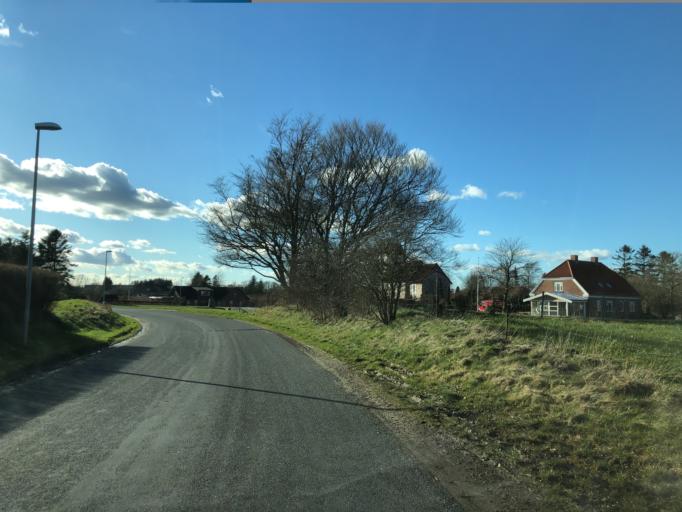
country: DK
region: Central Jutland
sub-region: Silkeborg Kommune
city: Kjellerup
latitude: 56.3326
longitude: 9.4861
